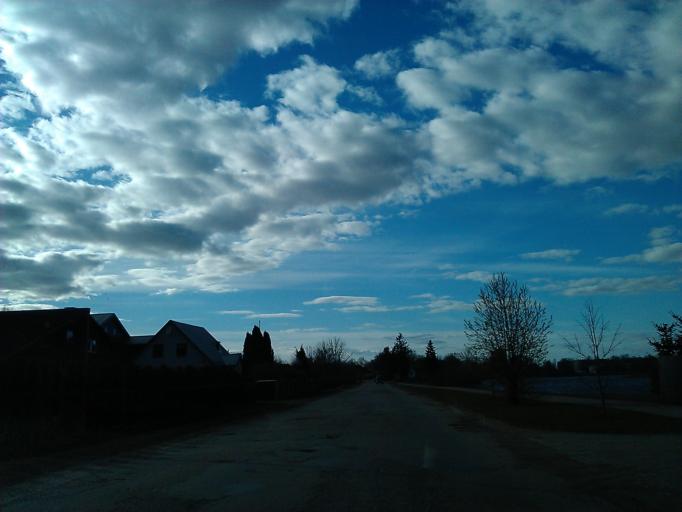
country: LV
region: Adazi
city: Adazi
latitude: 57.0715
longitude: 24.3355
